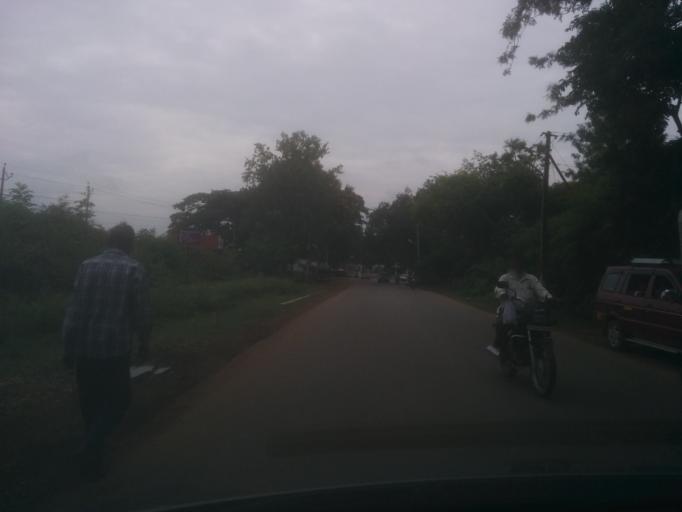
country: IN
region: Karnataka
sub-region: Chikmagalur
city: Chikmagalur
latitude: 13.3350
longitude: 75.7726
